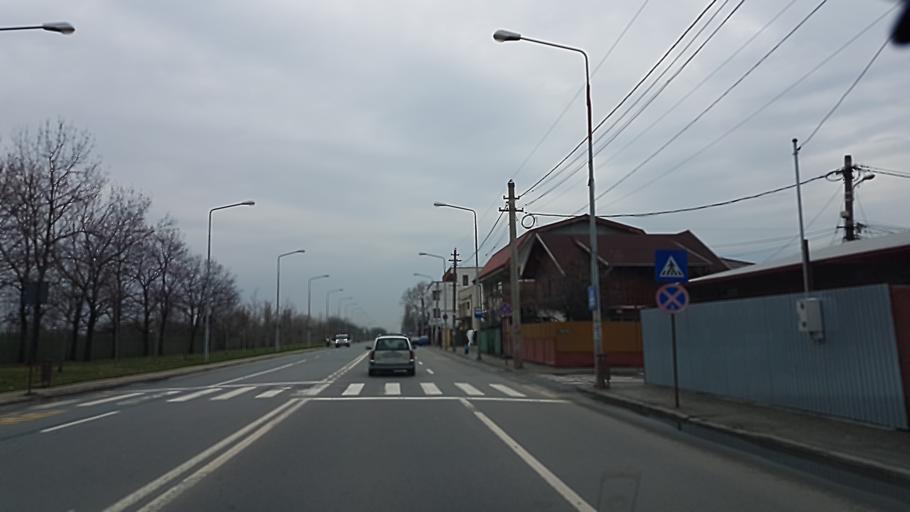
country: RO
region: Ilfov
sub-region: Comuna Pantelimon
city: Pantelimon
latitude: 44.4348
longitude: 26.2038
